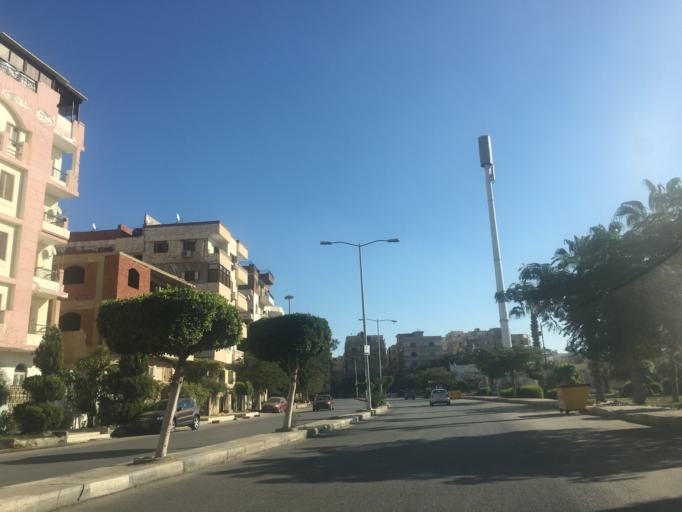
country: EG
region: Al Jizah
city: Madinat Sittah Uktubar
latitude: 29.9820
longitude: 30.9454
